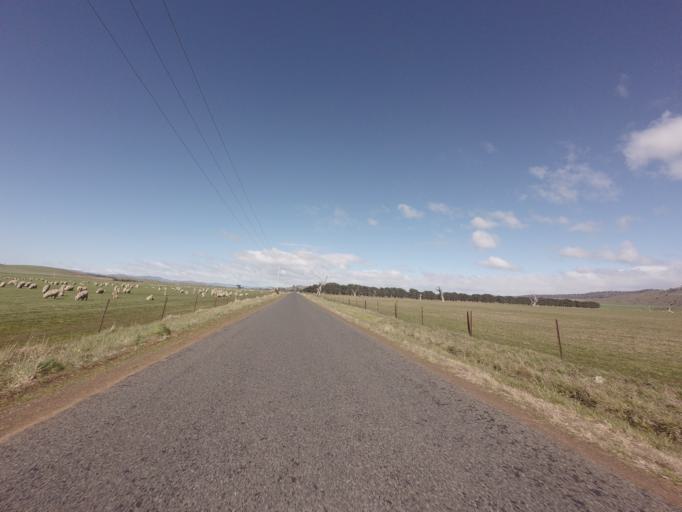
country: AU
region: Tasmania
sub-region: Northern Midlands
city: Evandale
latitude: -41.9907
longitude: 147.4525
